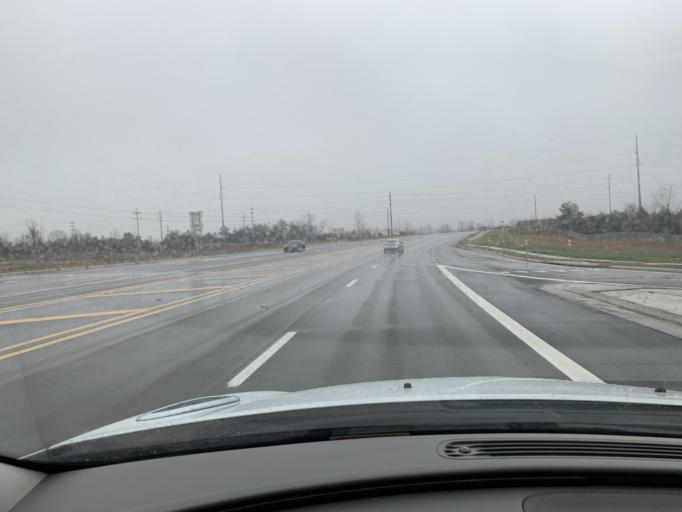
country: US
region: Mississippi
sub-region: De Soto County
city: Hernando
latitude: 34.8626
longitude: -89.9681
